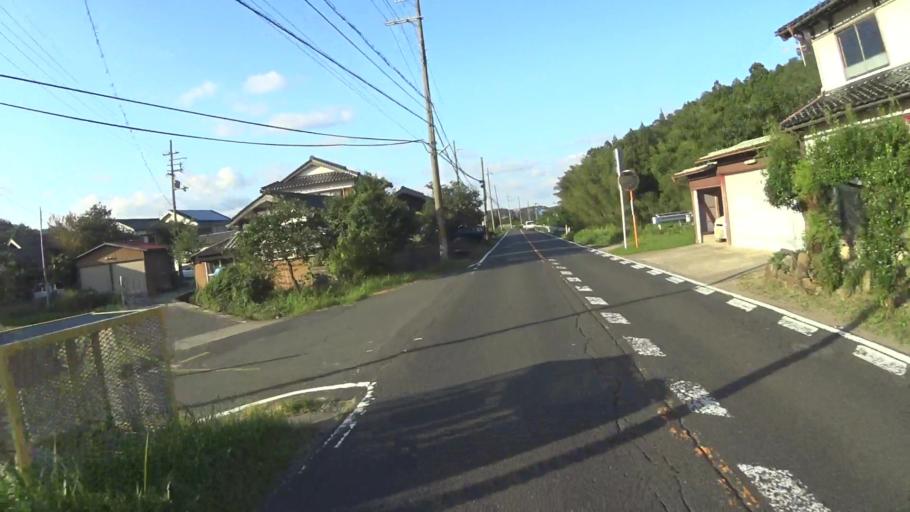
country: JP
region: Kyoto
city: Miyazu
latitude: 35.5948
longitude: 135.0435
